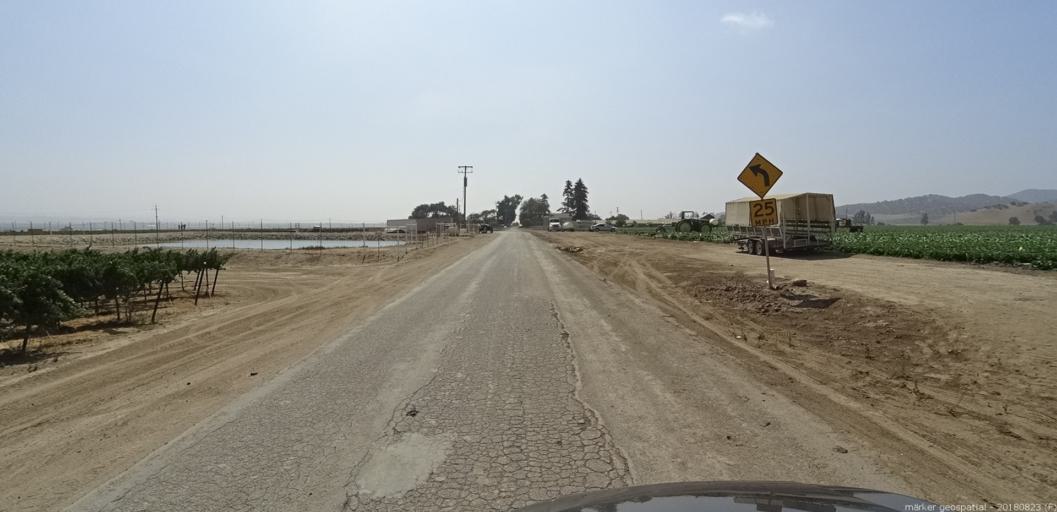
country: US
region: California
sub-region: Monterey County
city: King City
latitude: 36.2346
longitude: -121.1779
